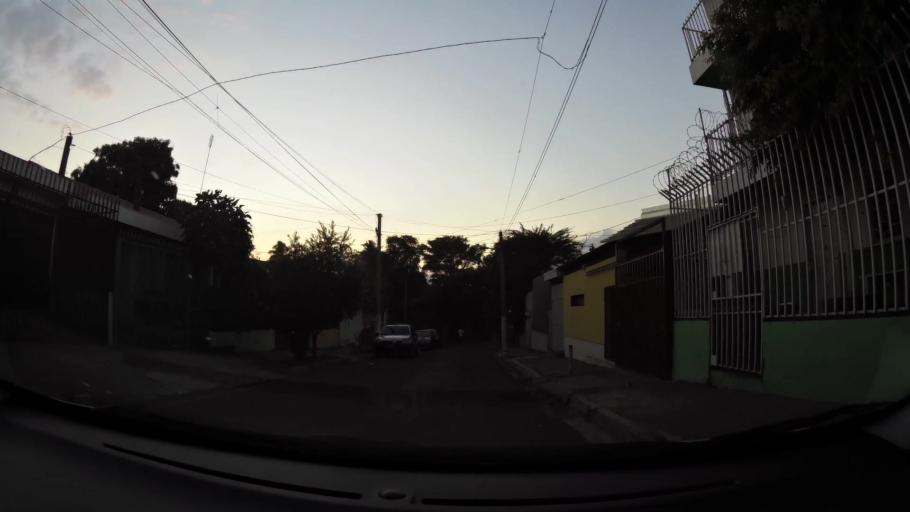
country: SV
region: San Salvador
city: San Salvador
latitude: 13.7042
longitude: -89.1834
